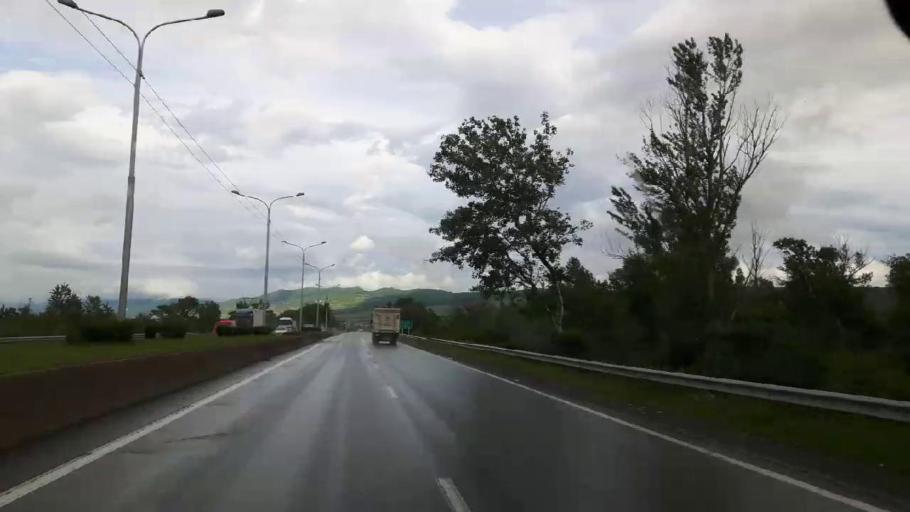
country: GE
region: Shida Kartli
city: Kaspi
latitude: 41.9095
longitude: 44.5693
